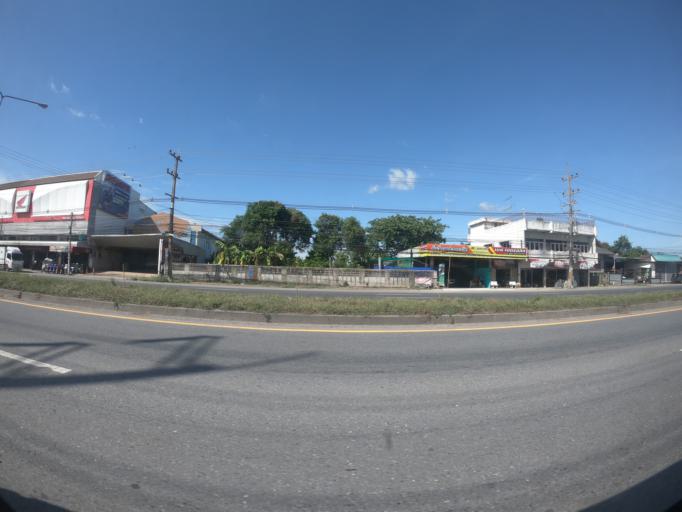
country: TH
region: Nakhon Nayok
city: Ban Na
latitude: 14.2577
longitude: 101.0776
